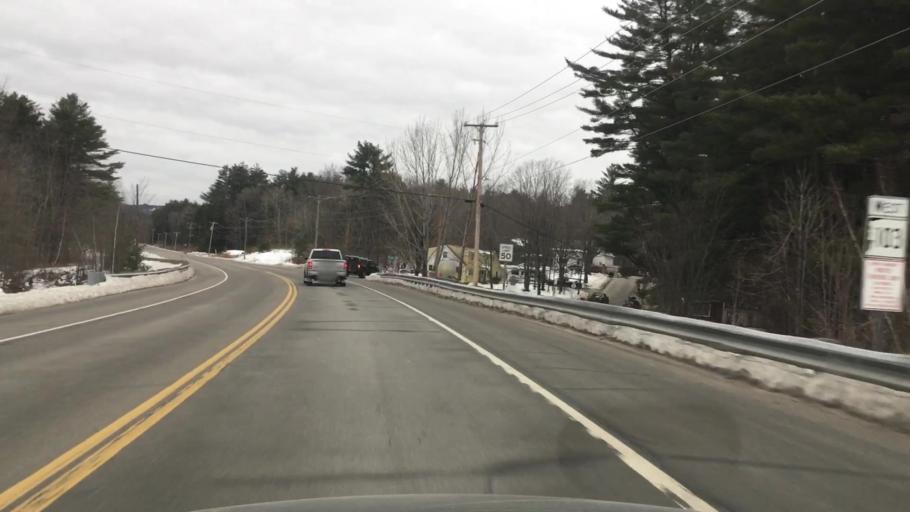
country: US
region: New Hampshire
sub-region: Merrimack County
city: Newbury
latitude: 43.2962
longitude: -71.9955
